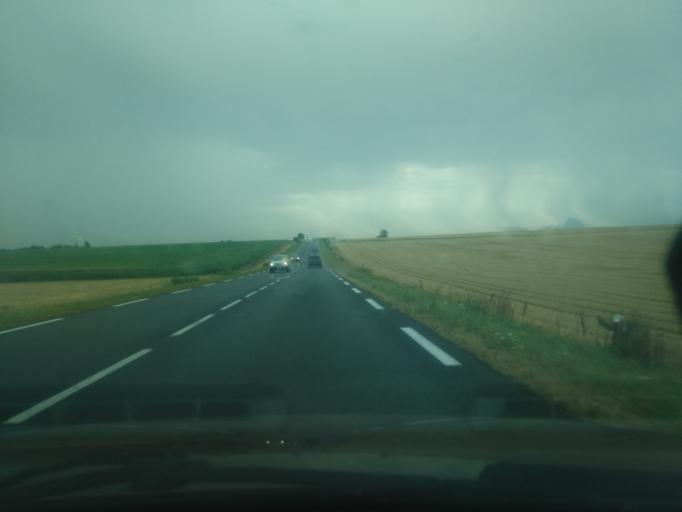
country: FR
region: Poitou-Charentes
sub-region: Departement de la Vienne
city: Cisse
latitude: 46.6346
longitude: 0.2281
